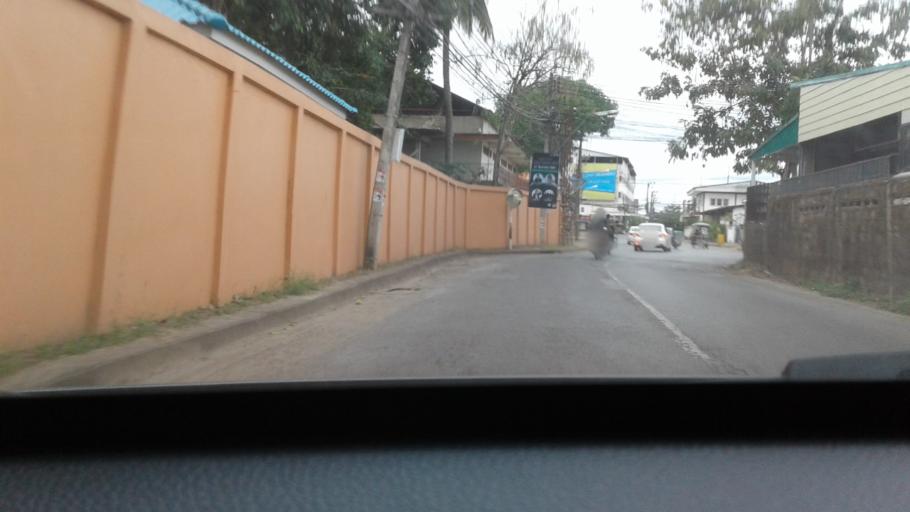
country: TH
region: Changwat Udon Thani
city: Udon Thani
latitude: 17.3981
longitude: 102.7842
